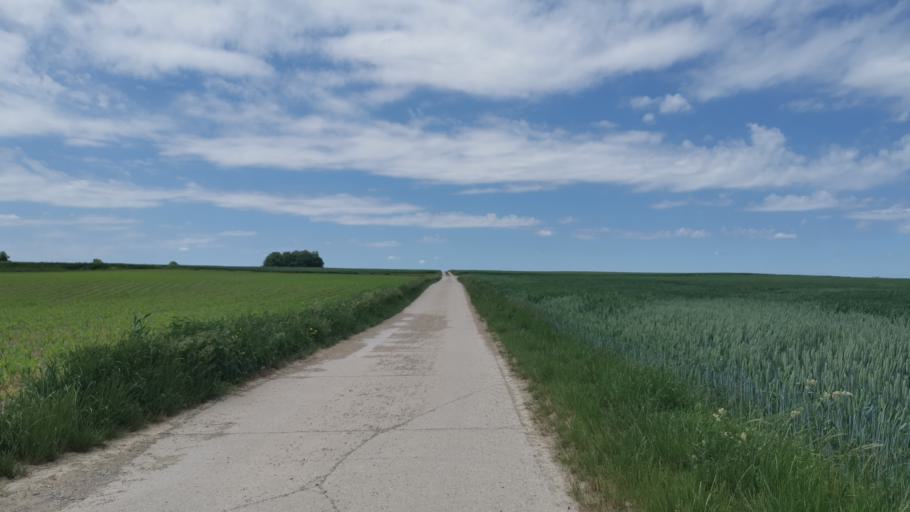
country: DE
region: Bavaria
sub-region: Swabia
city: Steindorf
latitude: 48.2397
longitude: 11.0116
